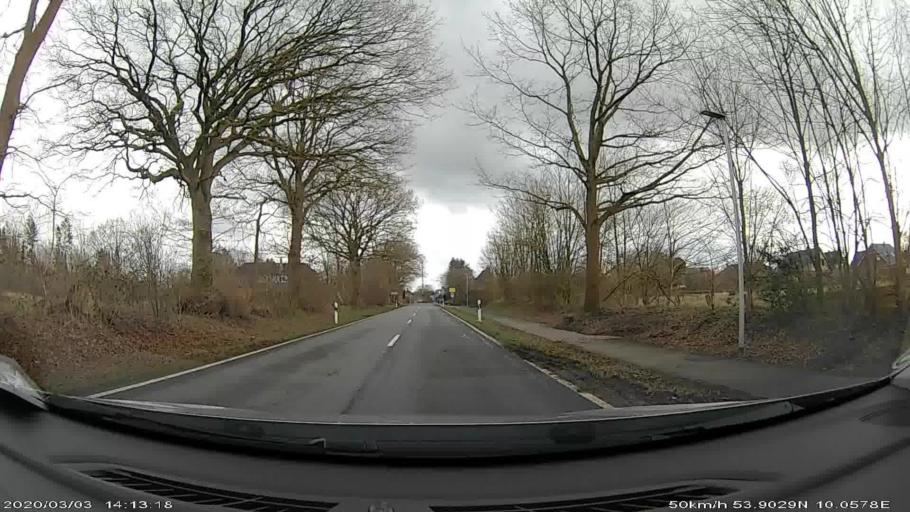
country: DE
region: Schleswig-Holstein
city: Hartenholm
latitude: 53.9027
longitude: 10.0583
